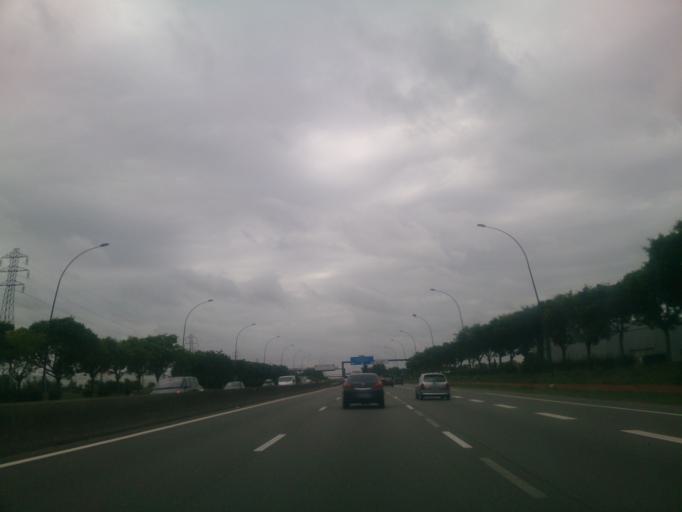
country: FR
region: Midi-Pyrenees
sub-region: Departement de la Haute-Garonne
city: Portet-sur-Garonne
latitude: 43.5589
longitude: 1.4141
